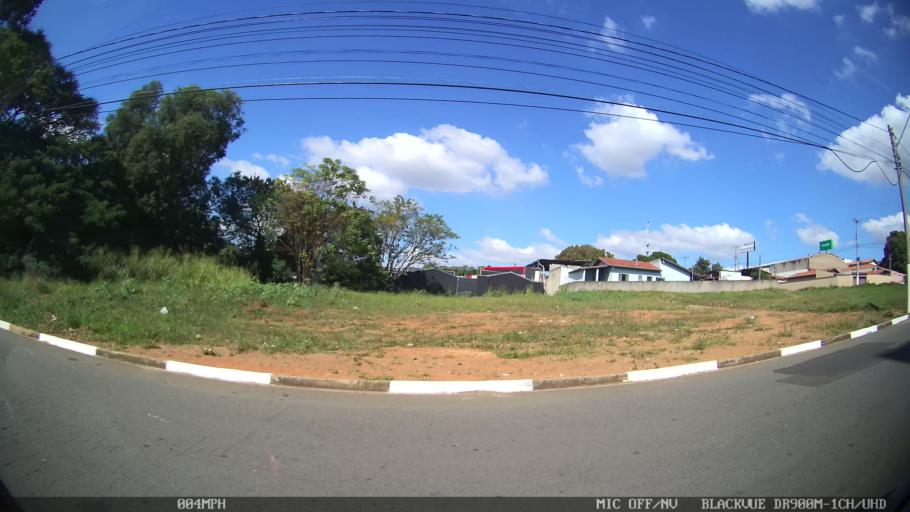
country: BR
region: Sao Paulo
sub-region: Hortolandia
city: Hortolandia
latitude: -22.8973
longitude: -47.1942
